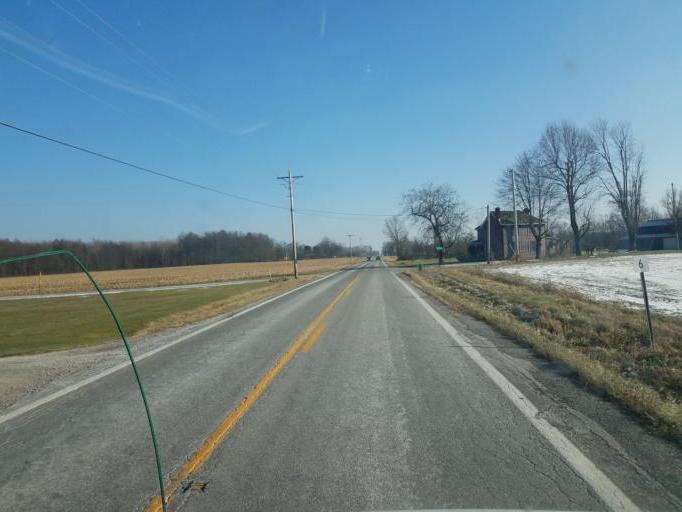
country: US
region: Ohio
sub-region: Marion County
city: Marion
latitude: 40.5429
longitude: -83.0151
